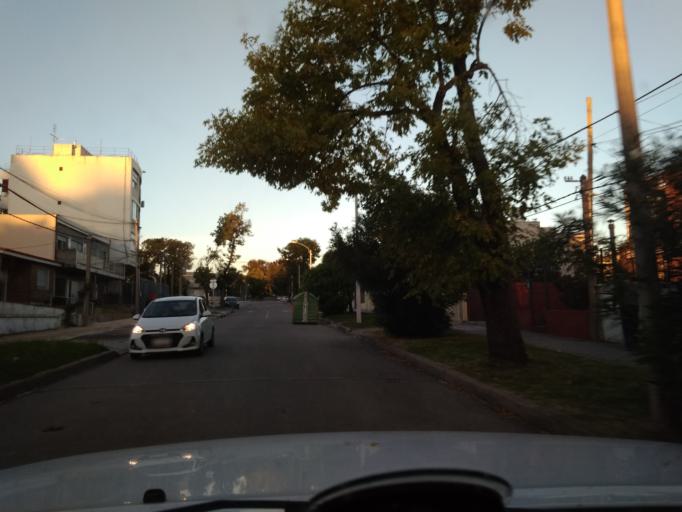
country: UY
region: Montevideo
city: Montevideo
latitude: -34.8928
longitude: -56.1174
